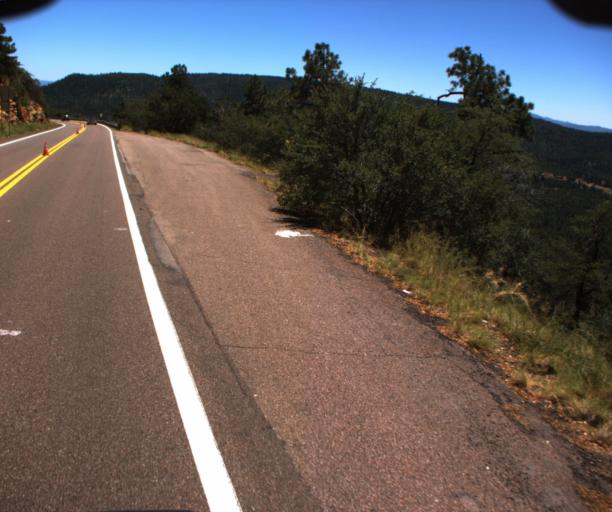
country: US
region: Arizona
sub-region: Gila County
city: Pine
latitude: 34.4212
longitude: -111.5082
